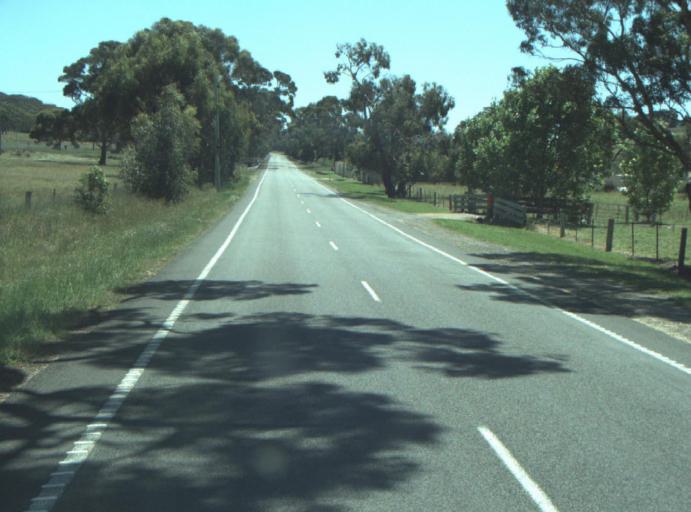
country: AU
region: Victoria
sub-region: Greater Geelong
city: Lara
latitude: -37.8914
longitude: 144.2557
